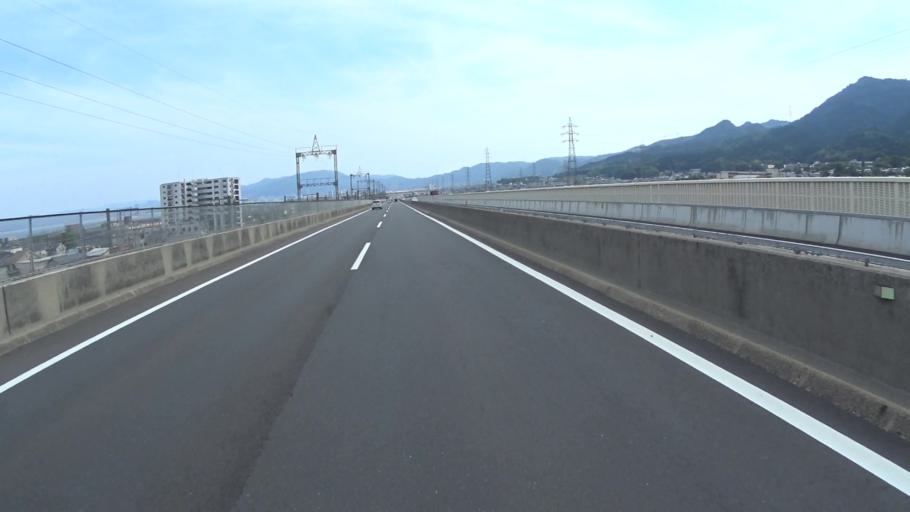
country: JP
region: Shiga Prefecture
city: Otsu-shi
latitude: 35.0728
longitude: 135.8792
